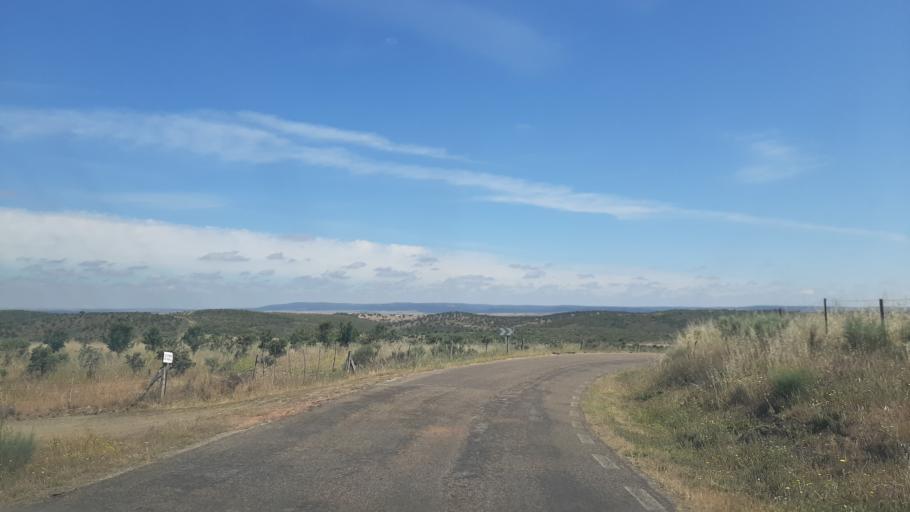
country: ES
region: Castille and Leon
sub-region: Provincia de Salamanca
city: Zamarra
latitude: 40.5254
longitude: -6.4640
